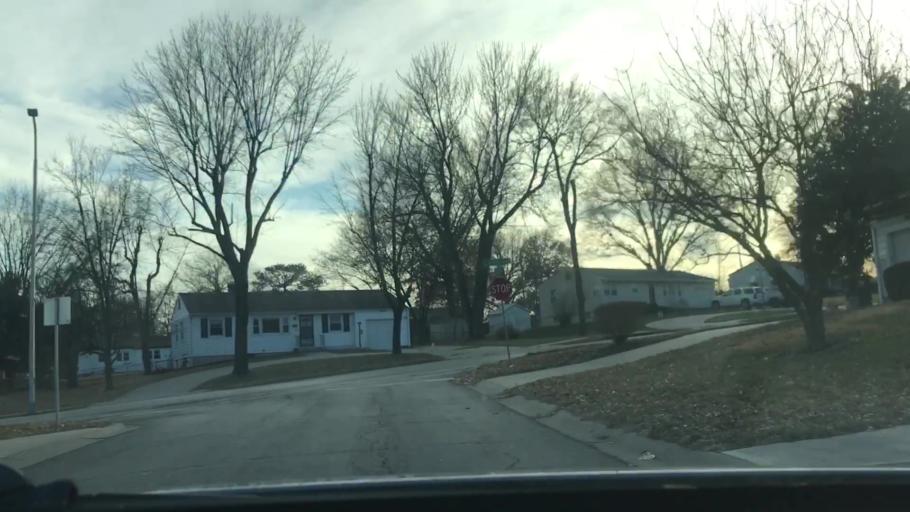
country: US
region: Missouri
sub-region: Jackson County
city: Independence
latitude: 39.0515
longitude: -94.4212
